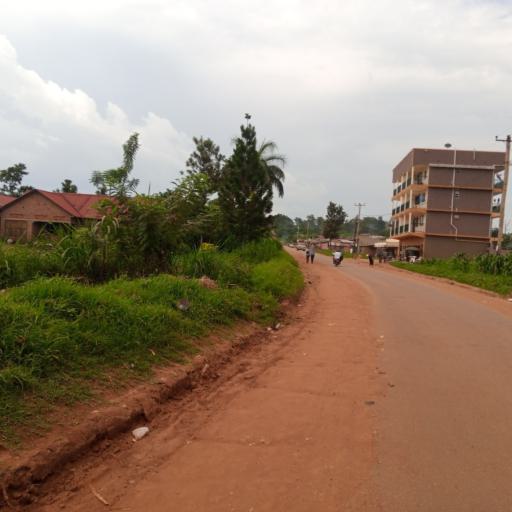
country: UG
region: Eastern Region
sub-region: Mbale District
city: Mbale
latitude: 1.0872
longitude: 34.1831
